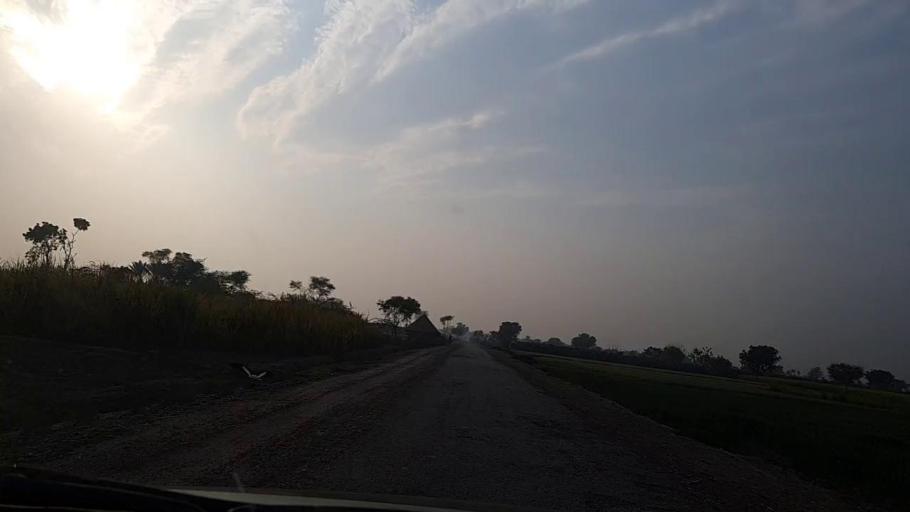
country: PK
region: Sindh
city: Nawabshah
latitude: 26.2833
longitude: 68.3301
